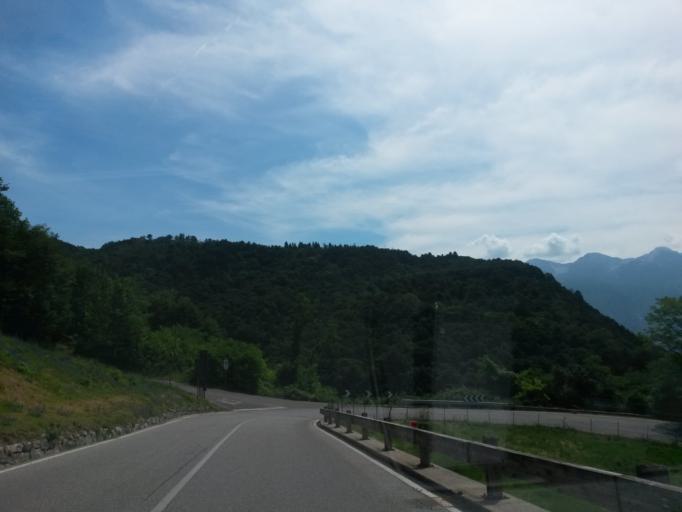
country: IT
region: Lombardy
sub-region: Provincia di Brescia
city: Pieve
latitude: 45.7896
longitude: 10.7503
